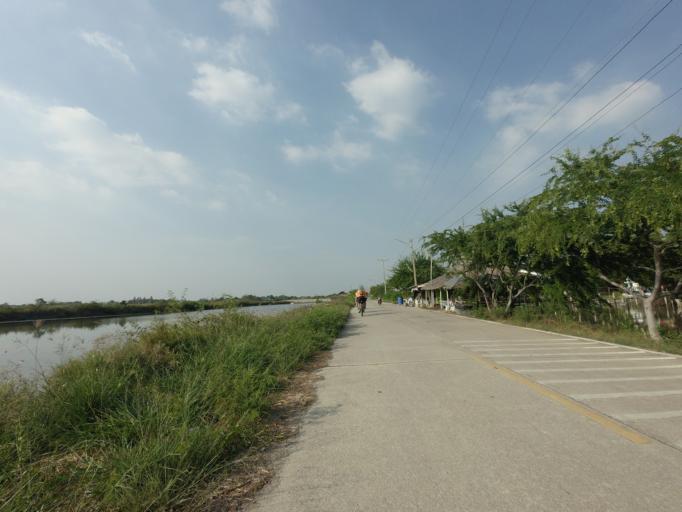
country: TH
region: Samut Sakhon
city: Samut Sakhon
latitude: 13.5004
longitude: 100.3281
